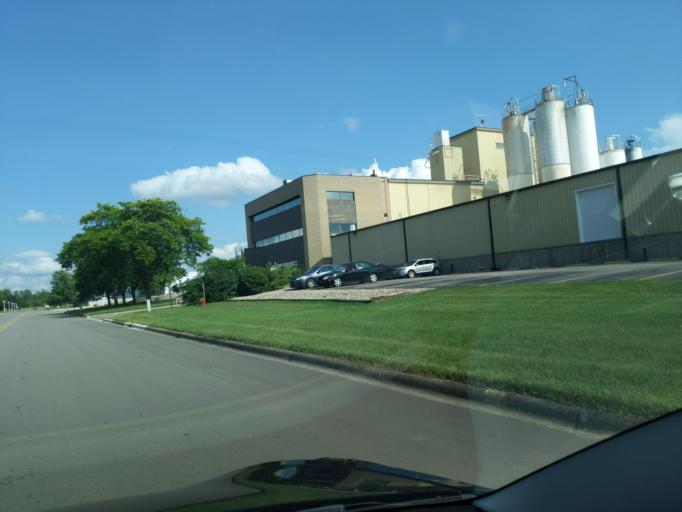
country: US
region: Michigan
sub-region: Jackson County
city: Jackson
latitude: 42.2264
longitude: -84.3682
